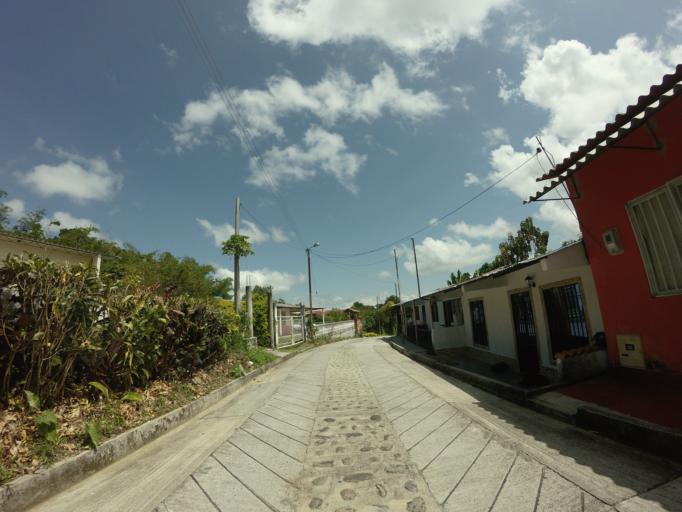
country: CO
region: Caldas
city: Victoria
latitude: 5.3195
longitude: -74.9185
